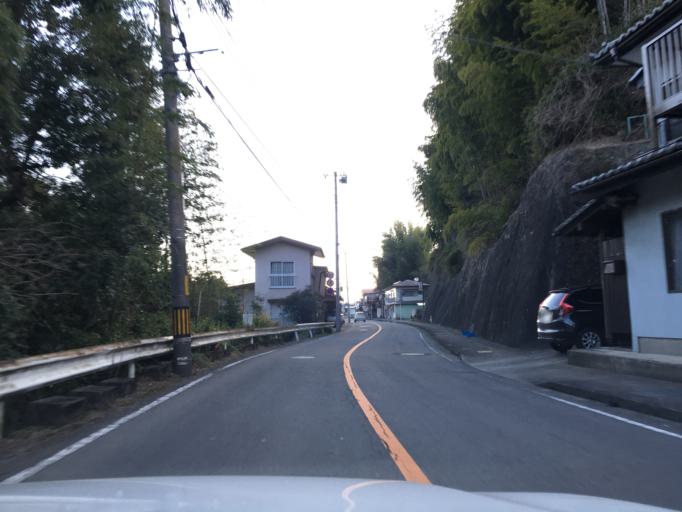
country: JP
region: Tochigi
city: Otawara
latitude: 36.8629
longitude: 140.1255
